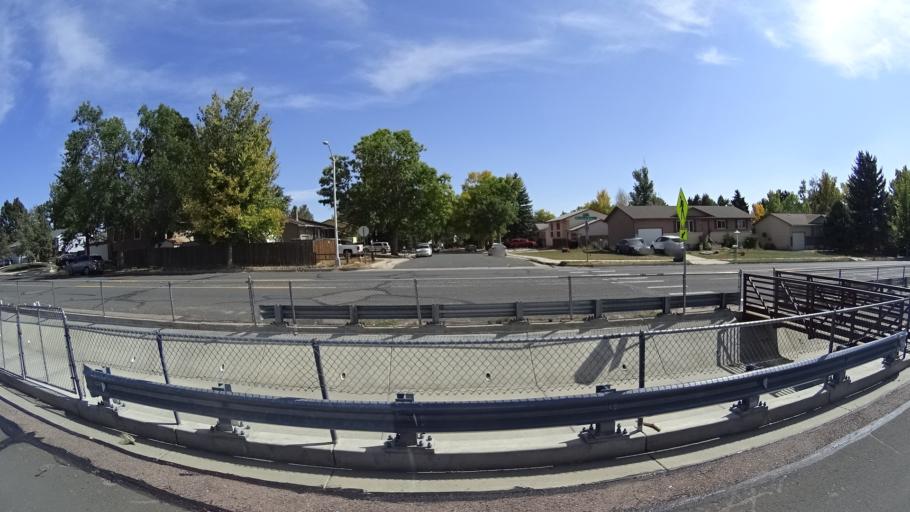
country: US
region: Colorado
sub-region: El Paso County
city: Cimarron Hills
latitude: 38.9022
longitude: -104.7569
